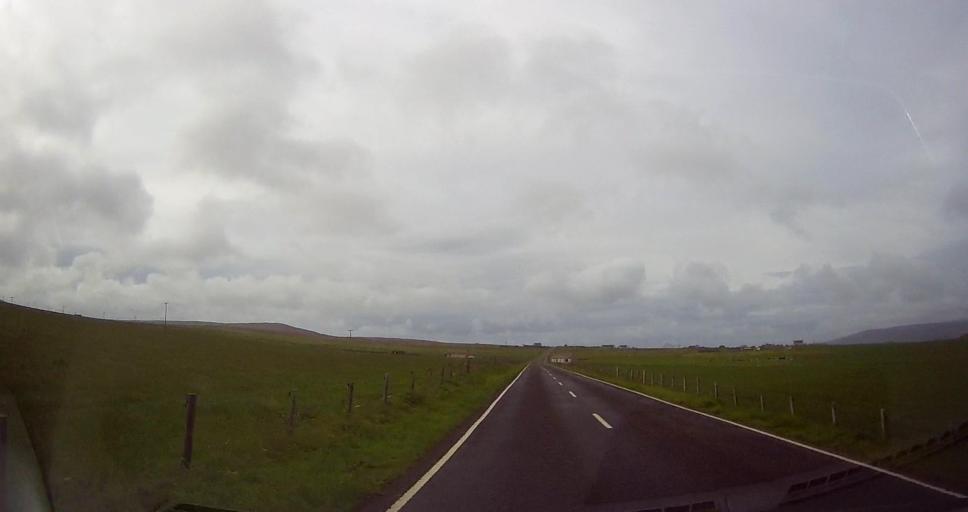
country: GB
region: Scotland
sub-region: Orkney Islands
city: Stromness
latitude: 58.9638
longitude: -3.2243
